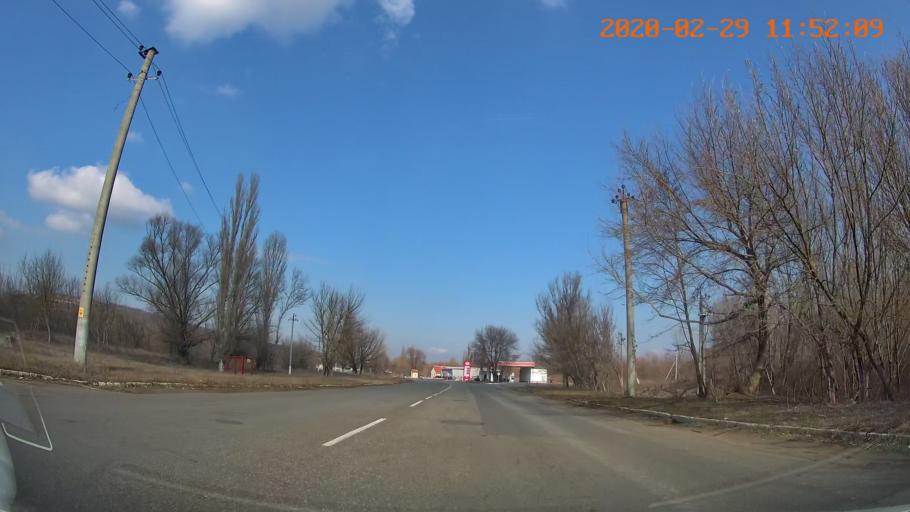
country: MD
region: Telenesti
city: Ribnita
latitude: 47.7703
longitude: 28.9913
